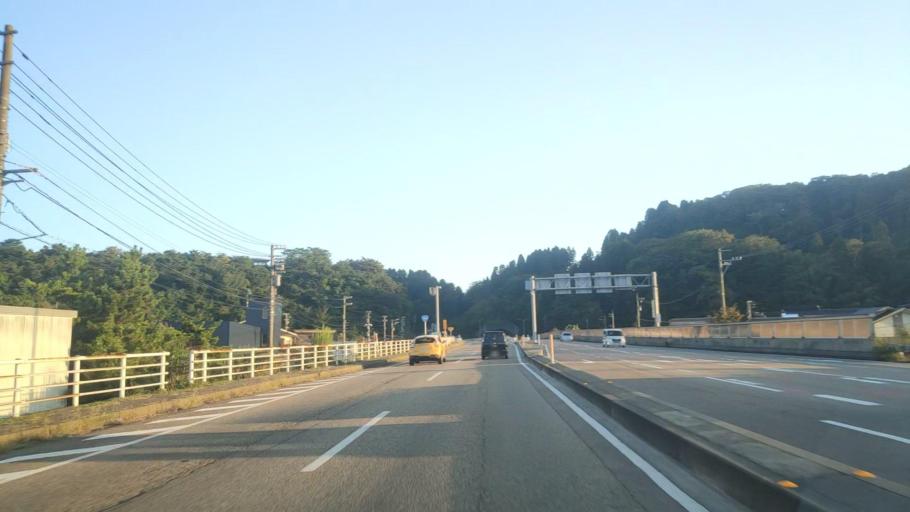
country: JP
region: Toyama
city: Himi
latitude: 36.8573
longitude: 136.9763
